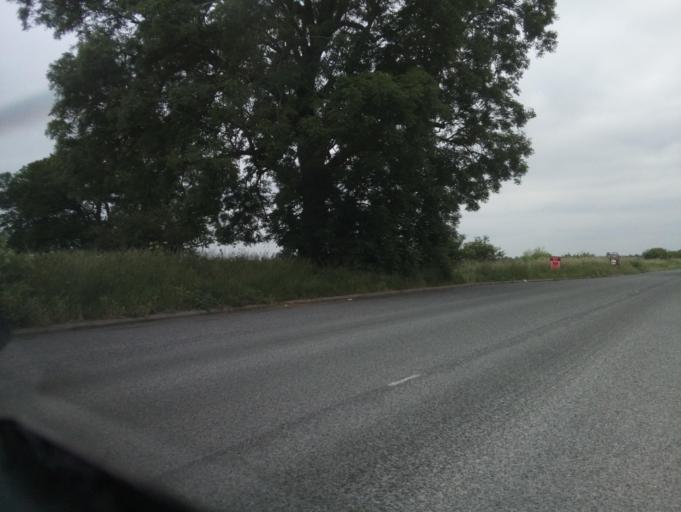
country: GB
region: England
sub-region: District of Rutland
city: Exton
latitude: 52.6730
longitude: -0.6534
